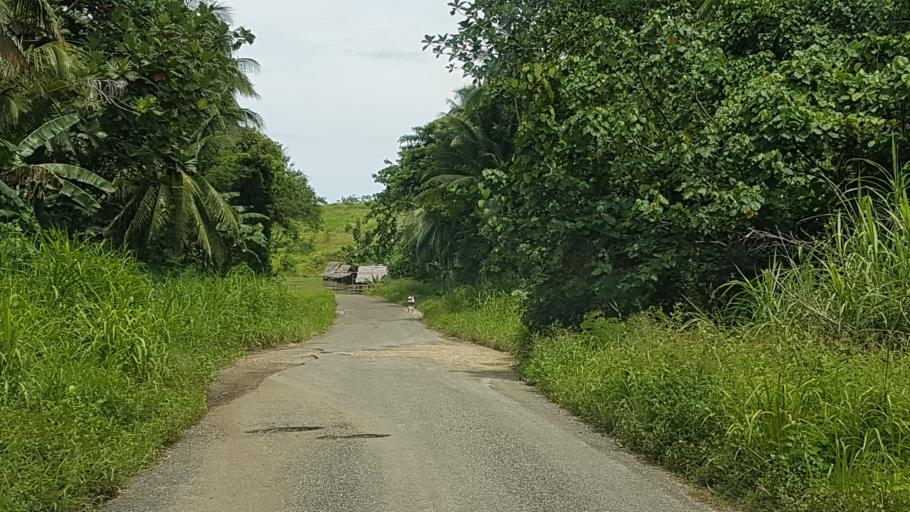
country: PG
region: Madang
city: Madang
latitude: -4.6064
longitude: 145.5508
